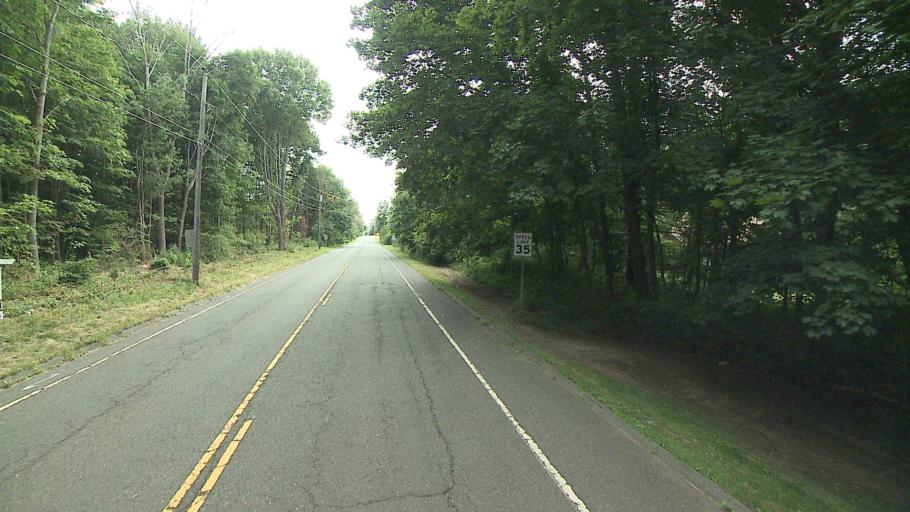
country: US
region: Connecticut
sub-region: Litchfield County
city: Bethlehem Village
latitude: 41.6433
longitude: -73.1957
